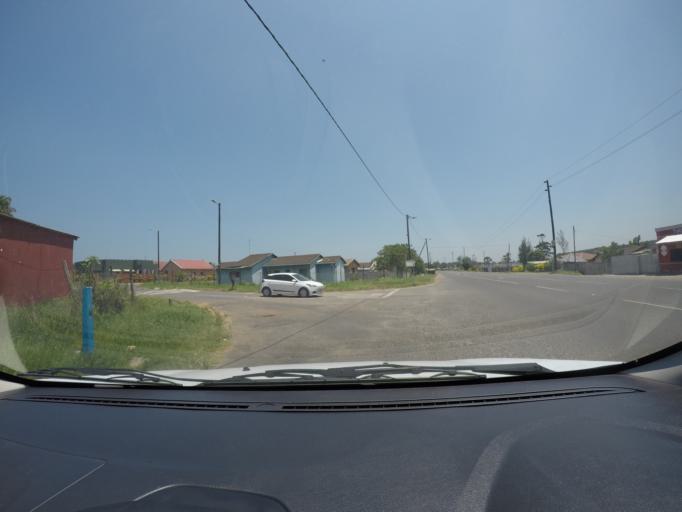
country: ZA
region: KwaZulu-Natal
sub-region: uThungulu District Municipality
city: eSikhawini
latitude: -28.8877
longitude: 31.8832
